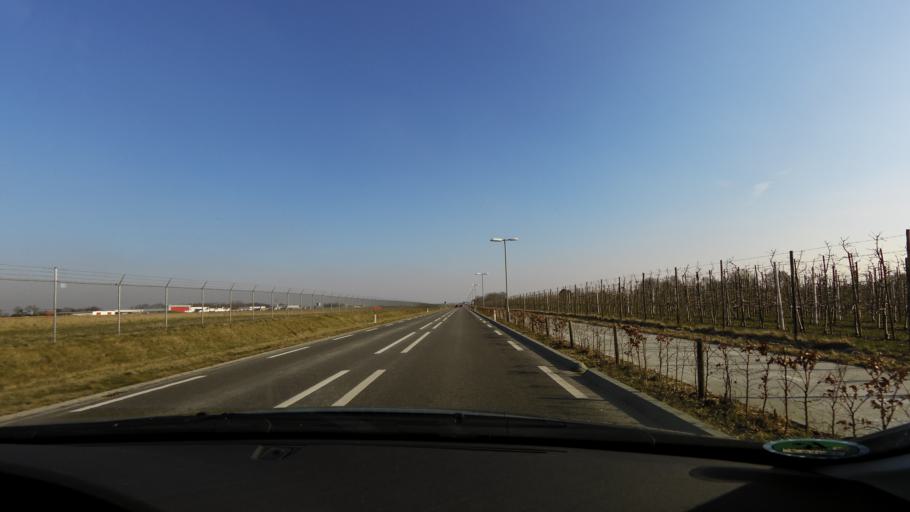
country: NL
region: Limburg
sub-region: Gemeente Meerssen
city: Meerssen
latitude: 50.9037
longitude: 5.7653
